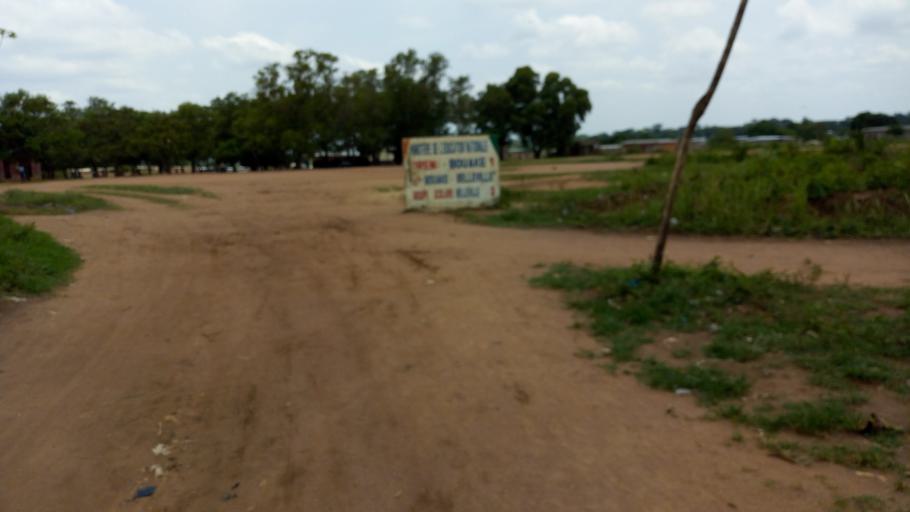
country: CI
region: Vallee du Bandama
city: Bouake
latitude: 7.7286
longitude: -4.9937
